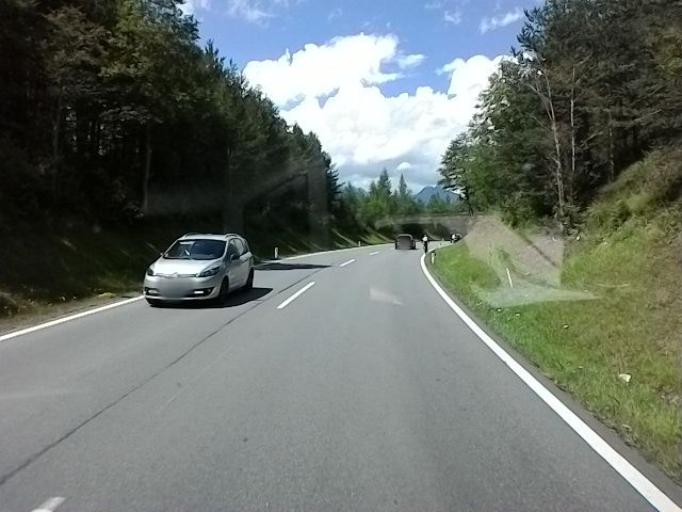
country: AT
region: Tyrol
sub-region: Politischer Bezirk Innsbruck Land
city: Reith bei Seefeld
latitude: 47.3170
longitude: 11.1991
